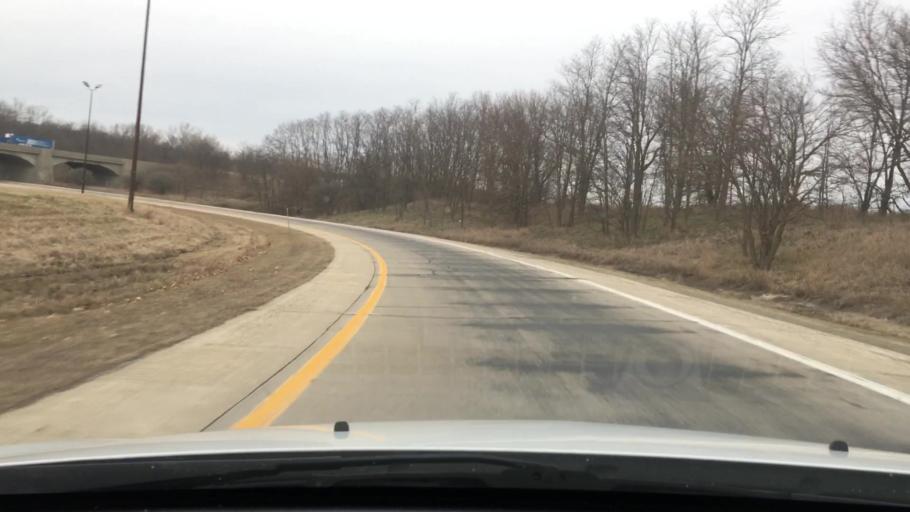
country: US
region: Illinois
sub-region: McLean County
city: Twin Grove
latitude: 40.3614
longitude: -89.1039
